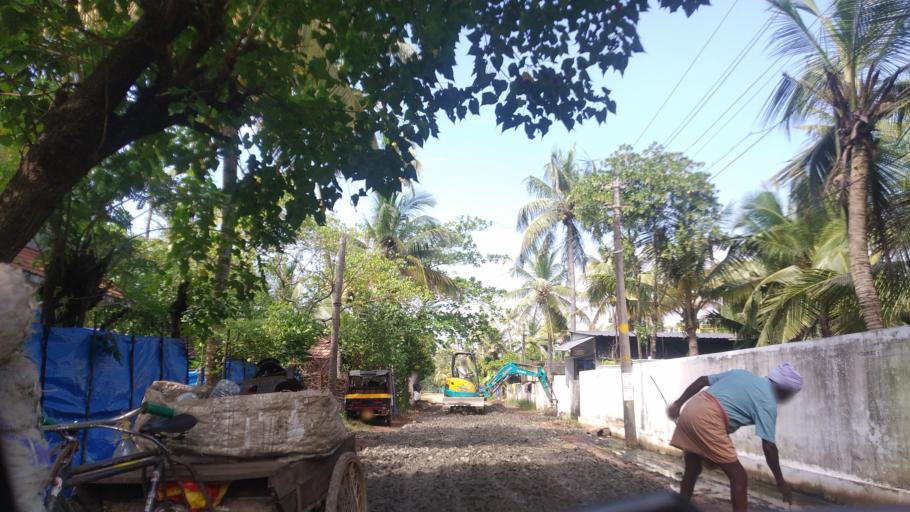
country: IN
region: Kerala
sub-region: Ernakulam
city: Elur
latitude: 10.0565
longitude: 76.2017
